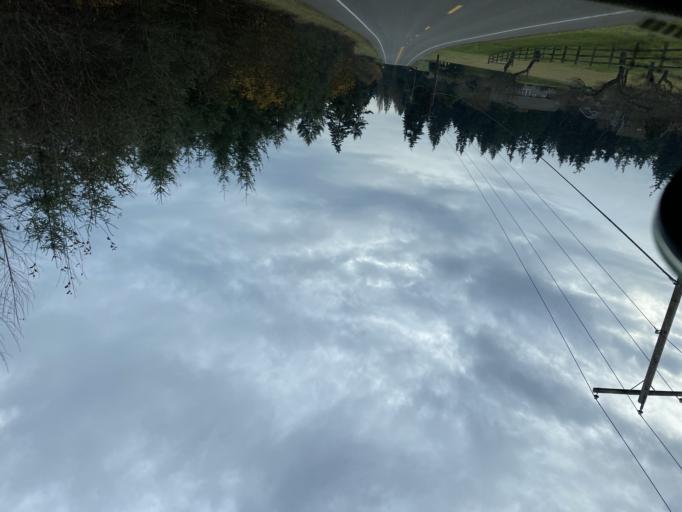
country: US
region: Washington
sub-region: Island County
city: Freeland
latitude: 48.0067
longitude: -122.5314
